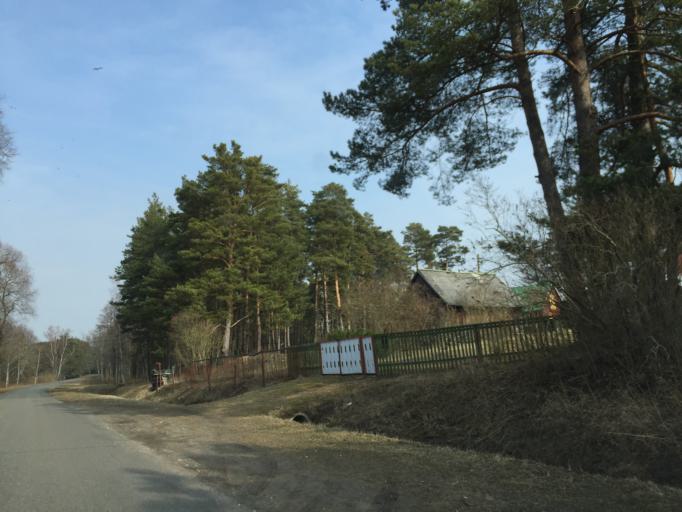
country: LV
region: Salacgrivas
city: Ainazi
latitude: 57.8794
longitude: 24.3636
